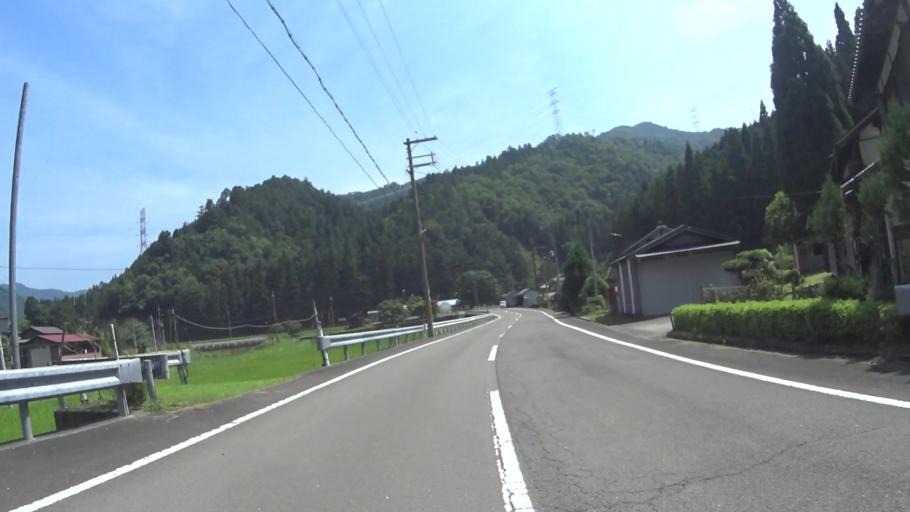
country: JP
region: Kyoto
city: Maizuru
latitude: 35.3315
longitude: 135.5391
